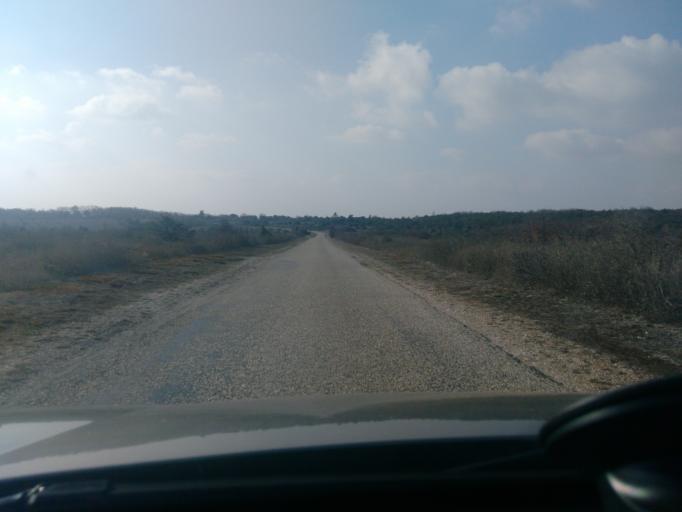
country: FR
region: Rhone-Alpes
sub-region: Departement de la Drome
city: Grignan
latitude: 44.4791
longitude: 4.8697
